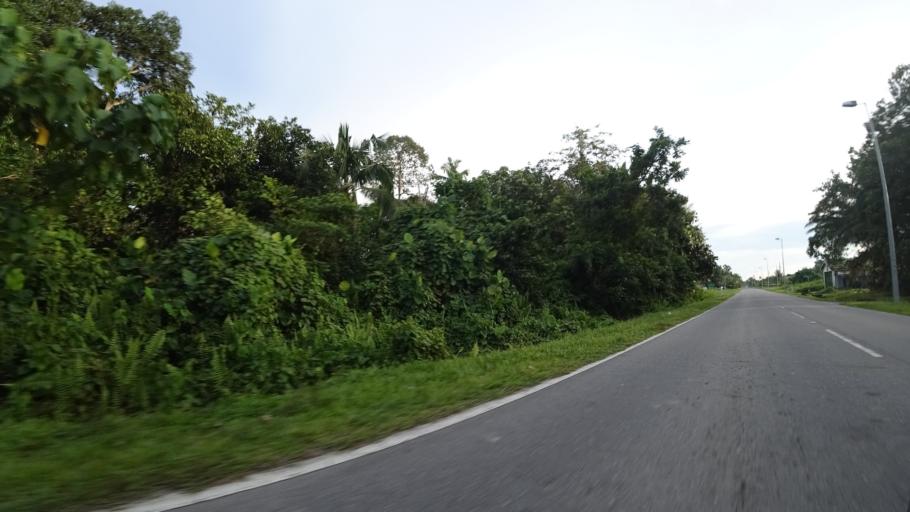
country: BN
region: Tutong
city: Tutong
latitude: 4.8185
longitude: 114.8165
